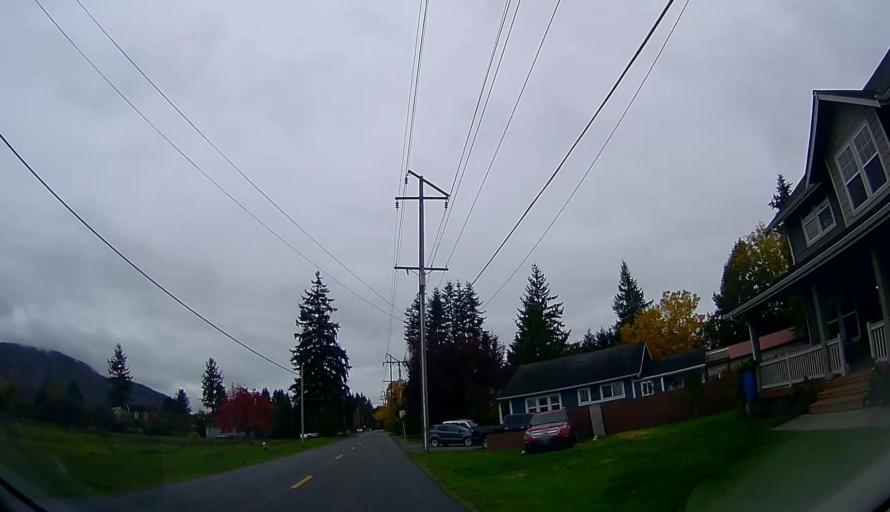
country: US
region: Washington
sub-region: Skagit County
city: Sedro-Woolley
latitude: 48.5021
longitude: -122.2153
